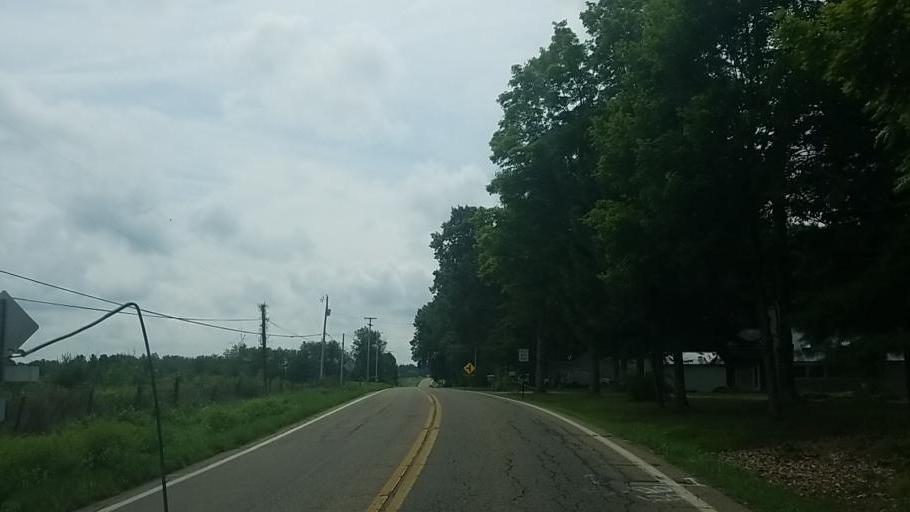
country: US
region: Ohio
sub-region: Knox County
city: Gambier
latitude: 40.3981
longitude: -82.4097
